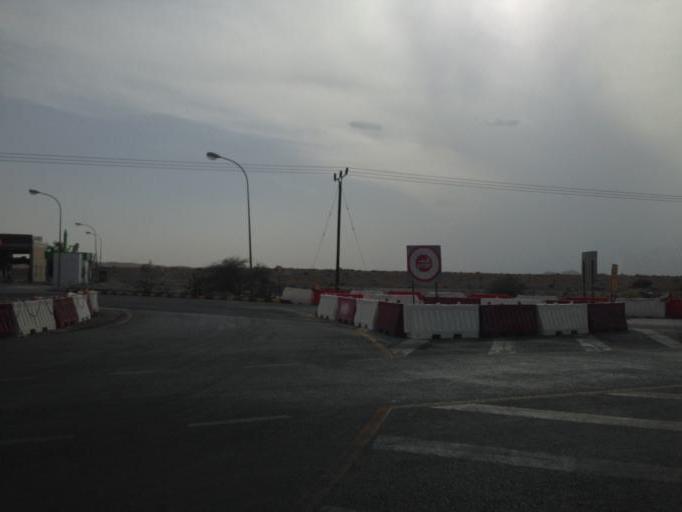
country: OM
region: Ash Sharqiyah
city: Al Qabil
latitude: 22.5335
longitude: 58.7317
